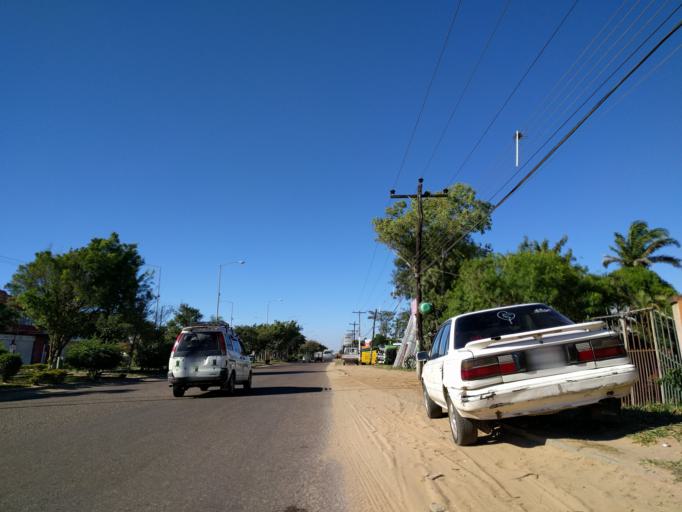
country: BO
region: Santa Cruz
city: Santa Cruz de la Sierra
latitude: -17.8443
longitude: -63.2448
